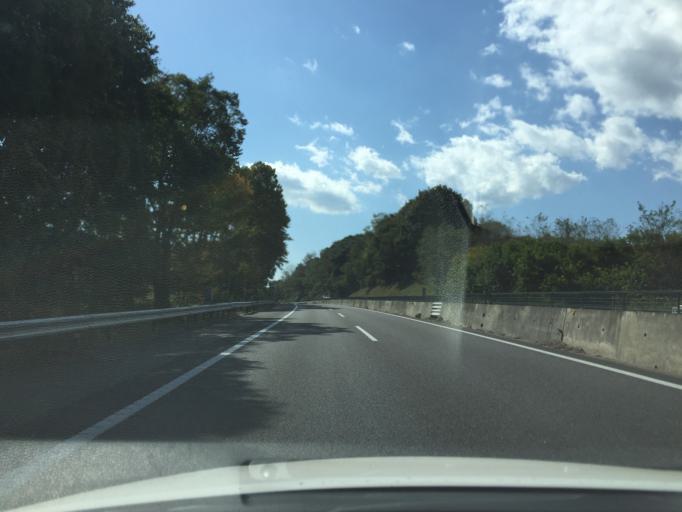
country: JP
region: Fukushima
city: Sukagawa
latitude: 37.2199
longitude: 140.3122
